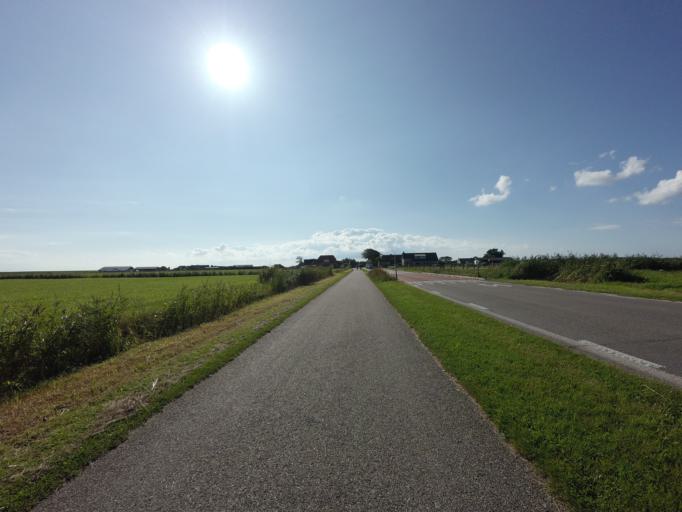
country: NL
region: Friesland
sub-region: Gemeente Terschelling
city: West-Terschelling
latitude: 53.3791
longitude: 5.2818
